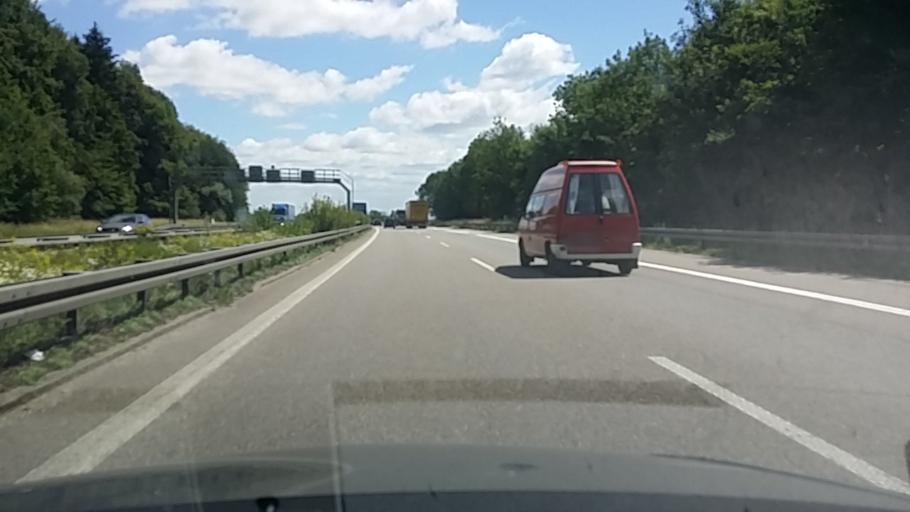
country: DE
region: Bavaria
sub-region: Swabia
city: Nersingen
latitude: 48.4547
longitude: 10.0690
